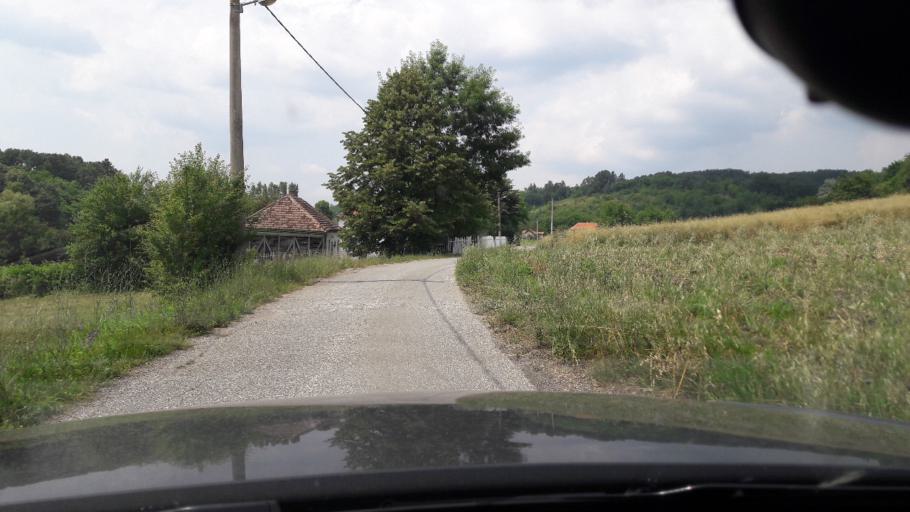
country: RS
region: Central Serbia
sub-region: Belgrade
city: Sopot
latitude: 44.6309
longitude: 20.5941
